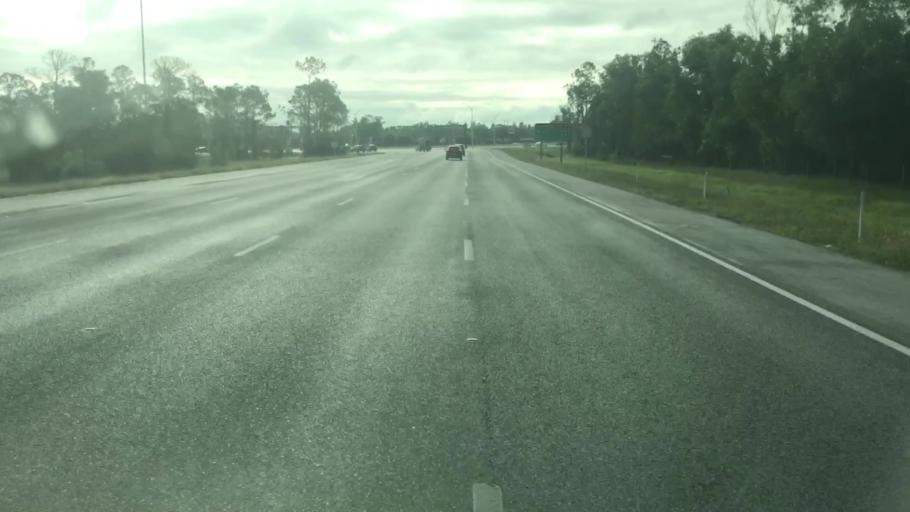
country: US
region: Florida
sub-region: Collier County
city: Golden Gate
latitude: 26.1597
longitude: -81.6886
